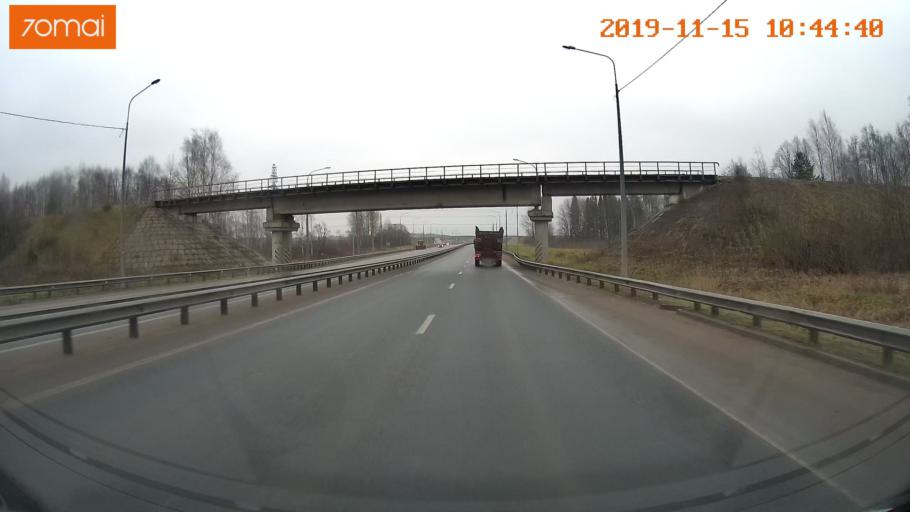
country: RU
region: Vologda
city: Sheksna
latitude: 59.2115
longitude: 38.5646
